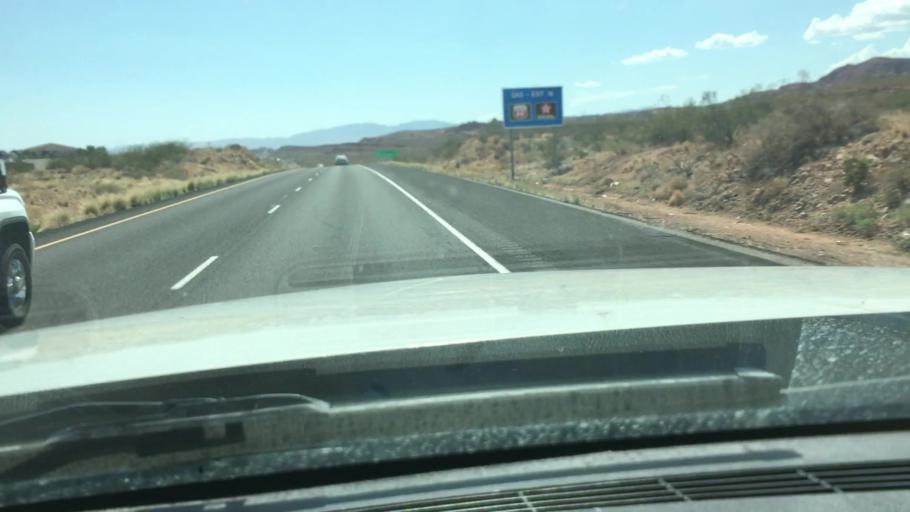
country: US
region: Utah
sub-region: Washington County
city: Washington
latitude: 37.1760
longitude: -113.4294
